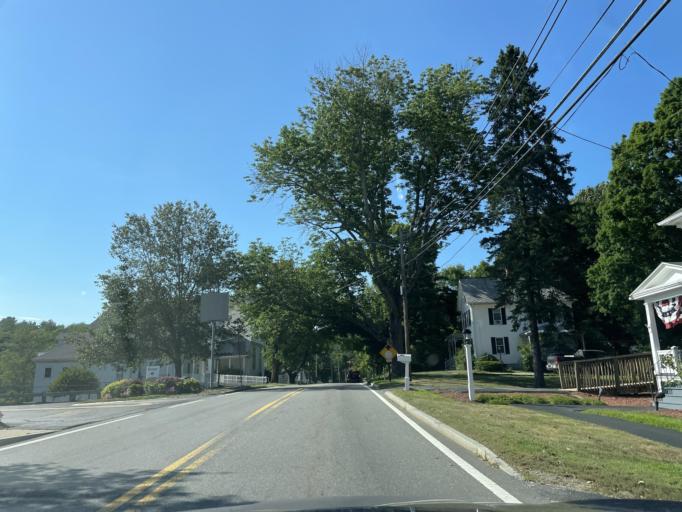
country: US
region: Massachusetts
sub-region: Worcester County
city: Charlton
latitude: 42.1462
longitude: -71.9874
